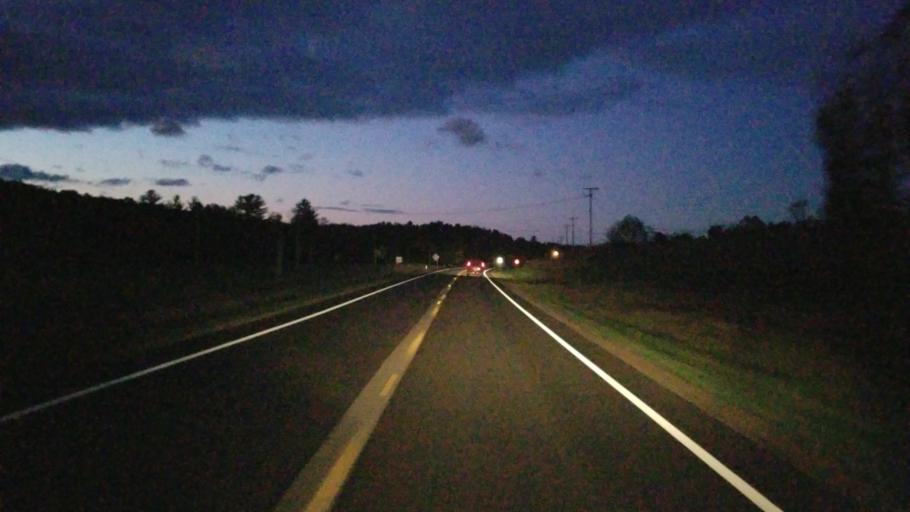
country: US
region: Ohio
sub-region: Vinton County
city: McArthur
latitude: 39.2797
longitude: -82.4682
